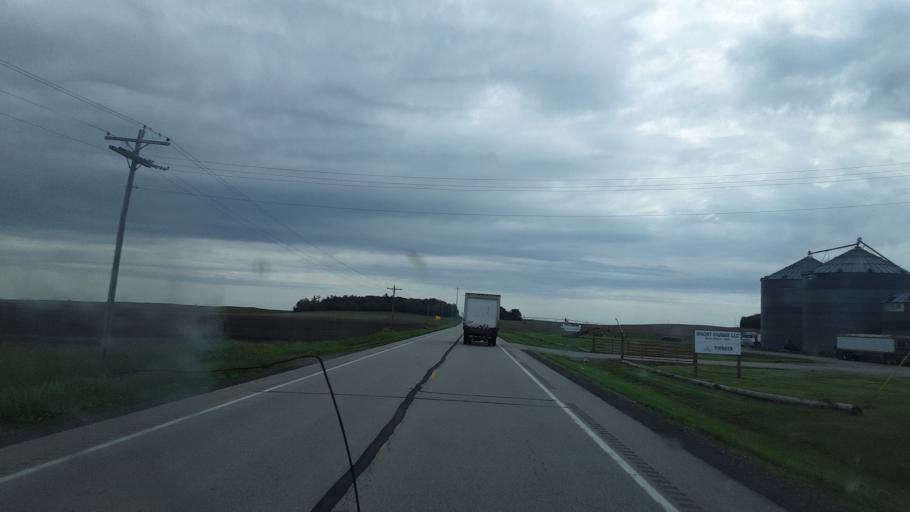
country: US
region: Illinois
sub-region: Mason County
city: Manito
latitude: 40.3034
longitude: -89.7915
